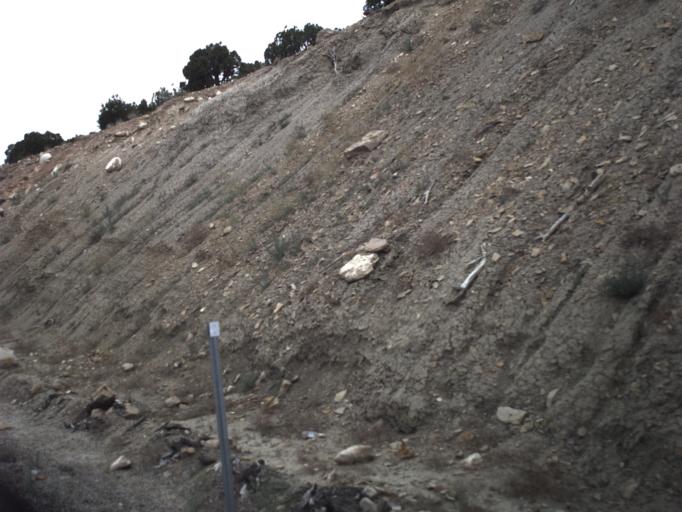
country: US
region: Utah
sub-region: Carbon County
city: East Carbon City
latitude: 39.4860
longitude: -110.4037
